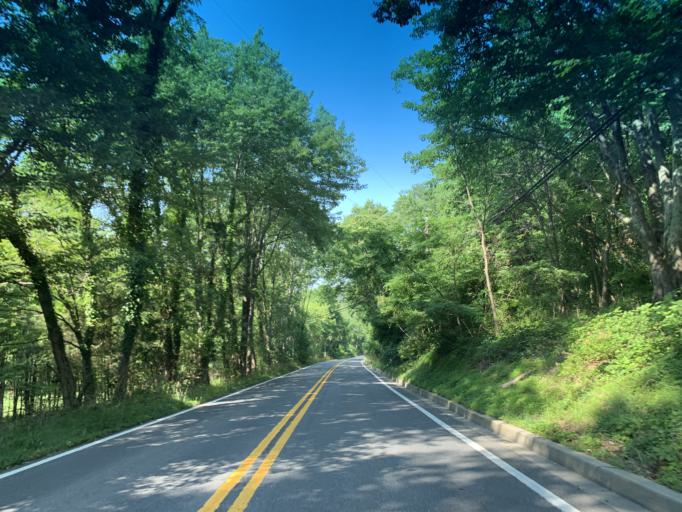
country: US
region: Maryland
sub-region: Montgomery County
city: Poolesville
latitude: 39.2251
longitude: -77.3734
